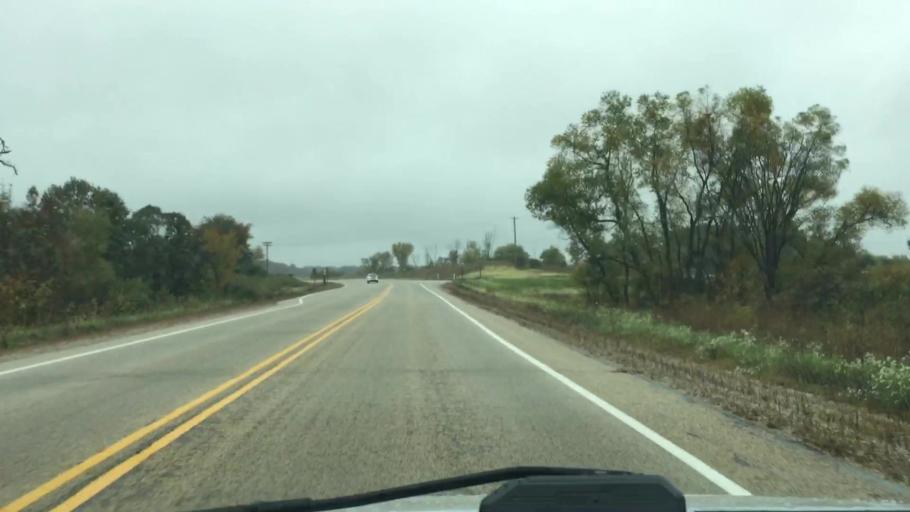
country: US
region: Wisconsin
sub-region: Jefferson County
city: Palmyra
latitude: 42.8840
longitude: -88.5590
